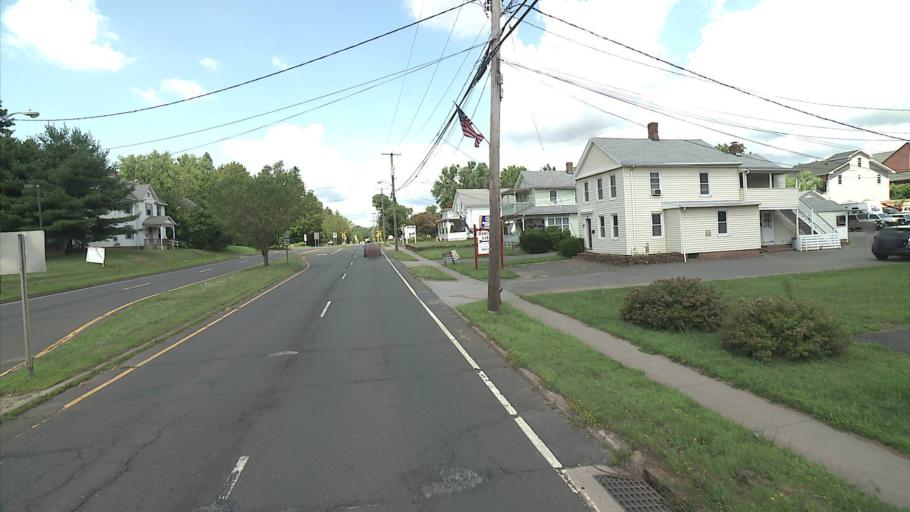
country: US
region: Connecticut
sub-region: Middlesex County
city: Portland
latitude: 41.5712
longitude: -72.6356
